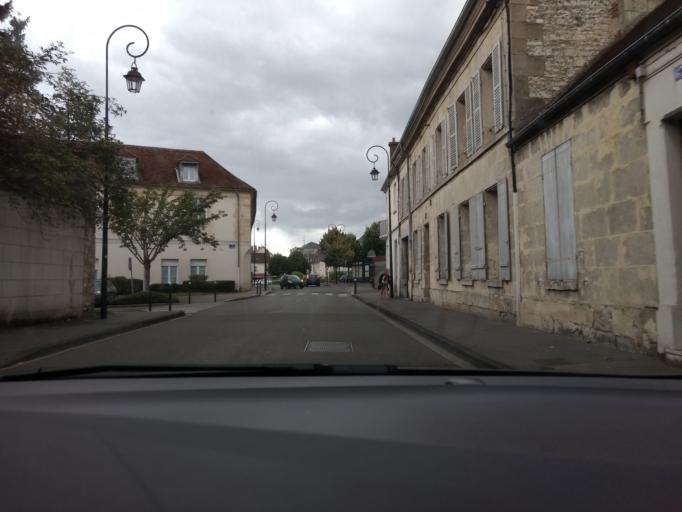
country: FR
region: Picardie
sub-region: Departement de l'Oise
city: Compiegne
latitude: 49.4125
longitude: 2.8206
